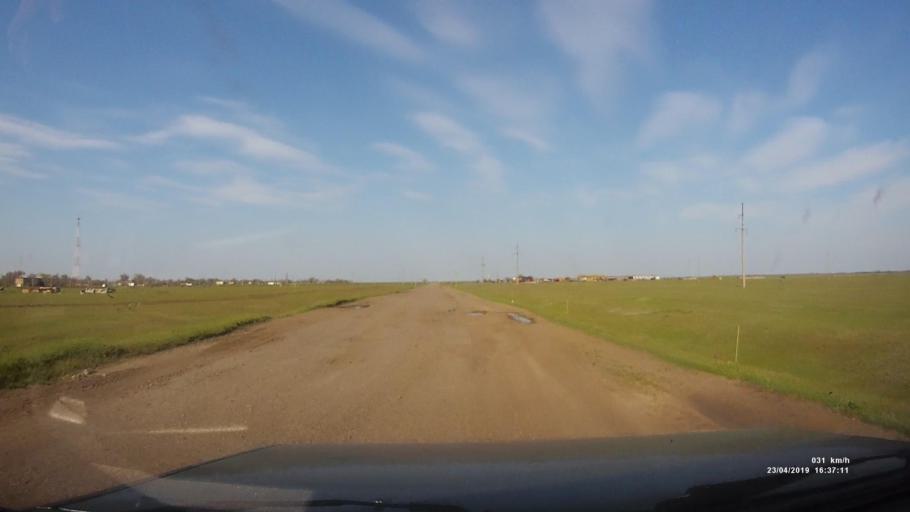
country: RU
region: Kalmykiya
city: Priyutnoye
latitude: 46.3319
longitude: 43.1458
